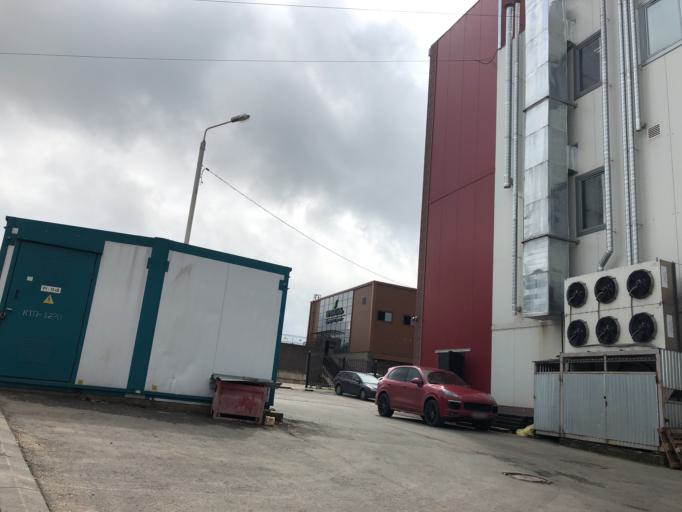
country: RU
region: Tula
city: Mendeleyevskiy
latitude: 54.1580
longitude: 37.5820
